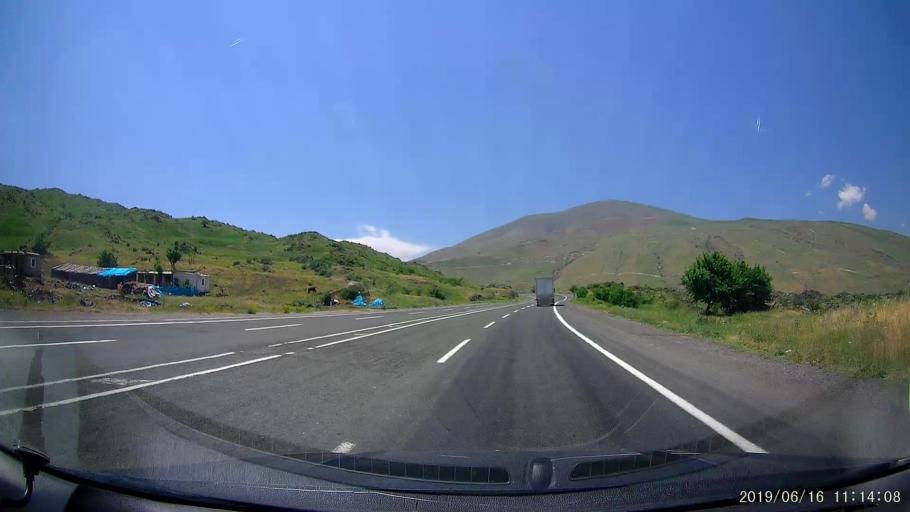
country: TR
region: Igdir
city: Igdir
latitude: 39.7829
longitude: 44.1452
